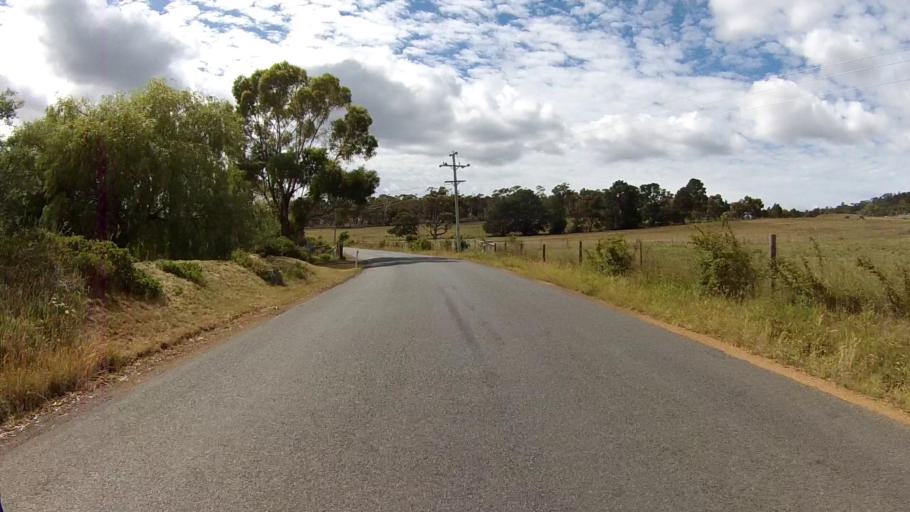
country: AU
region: Tasmania
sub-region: Clarence
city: Cambridge
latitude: -42.7653
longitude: 147.3934
